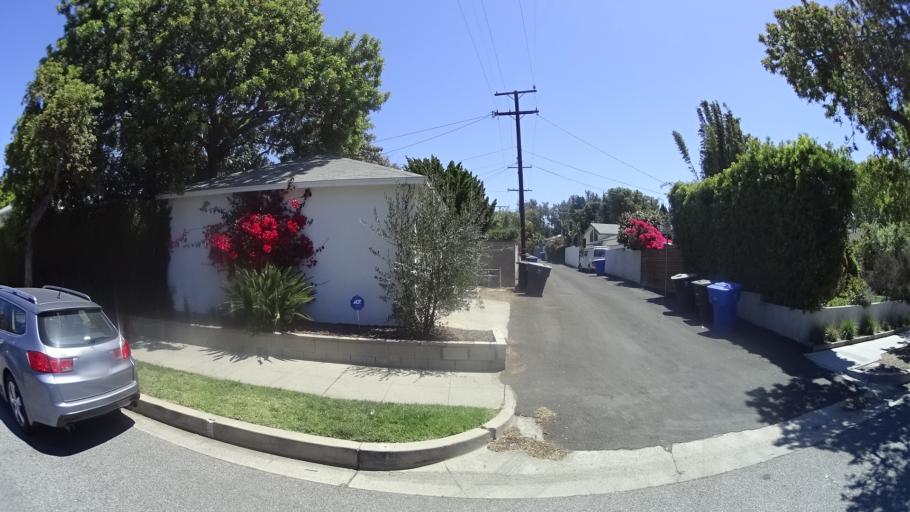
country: US
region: California
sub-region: Los Angeles County
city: Santa Monica
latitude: 34.0195
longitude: -118.4610
